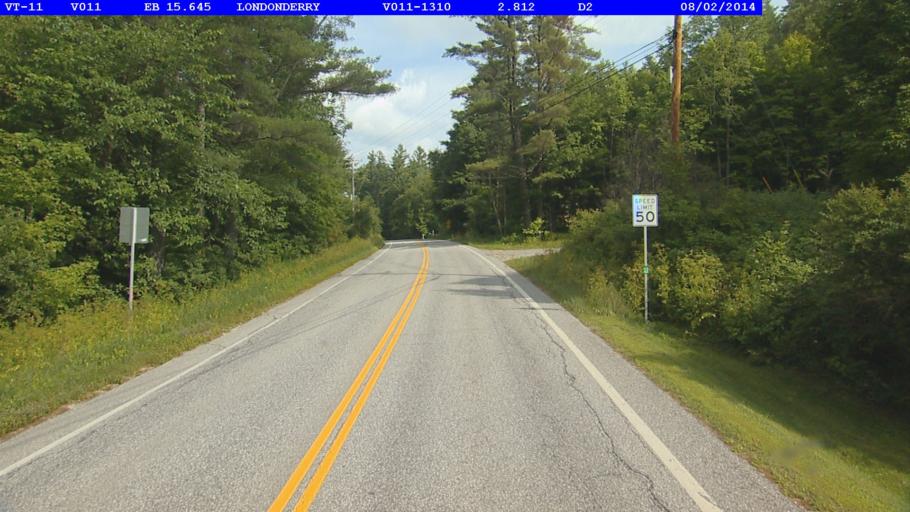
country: US
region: Vermont
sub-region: Windsor County
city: Chester
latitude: 43.2243
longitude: -72.7994
